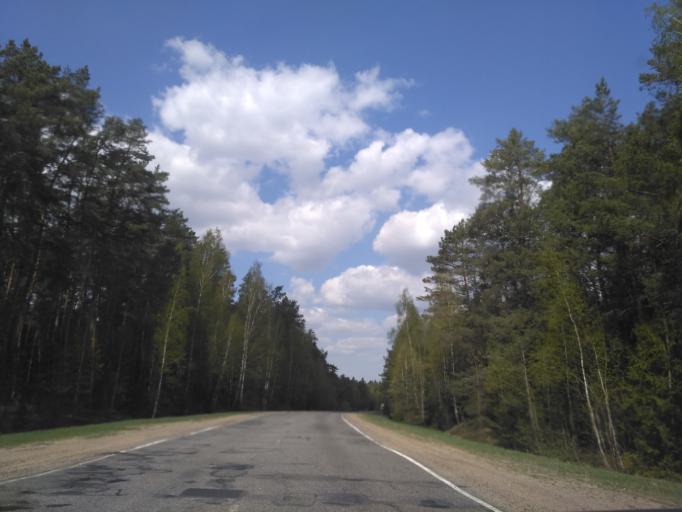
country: BY
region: Minsk
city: Il'ya
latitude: 54.4891
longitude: 27.2393
